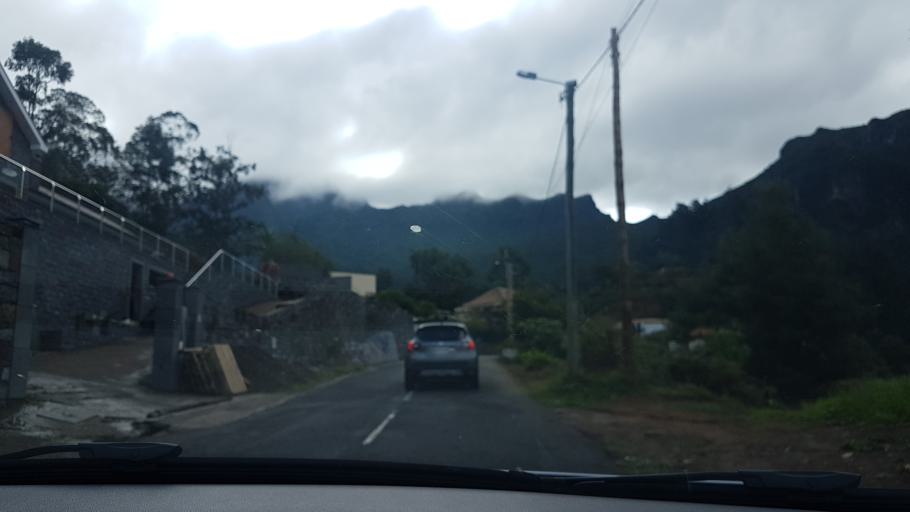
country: PT
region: Madeira
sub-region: Sao Vicente
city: Sao Vicente
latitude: 32.7764
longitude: -17.0280
